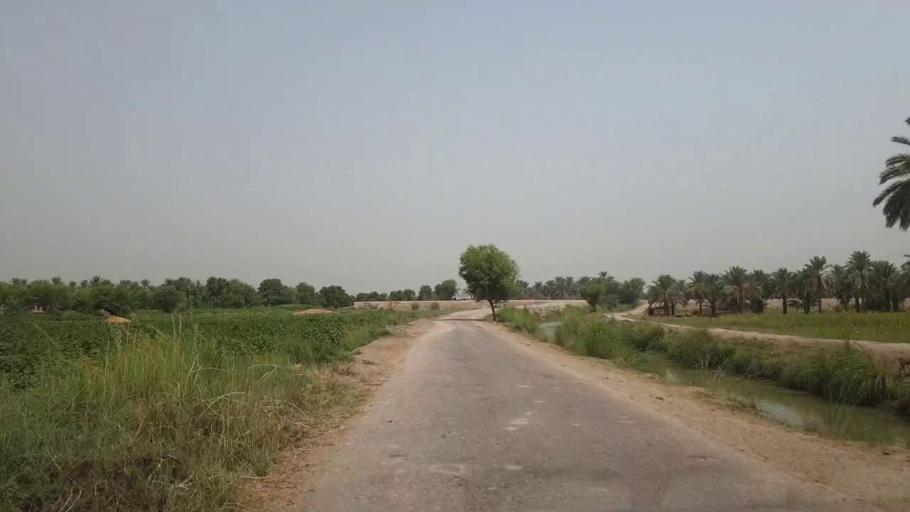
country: PK
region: Sindh
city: Gambat
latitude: 27.4357
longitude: 68.5596
